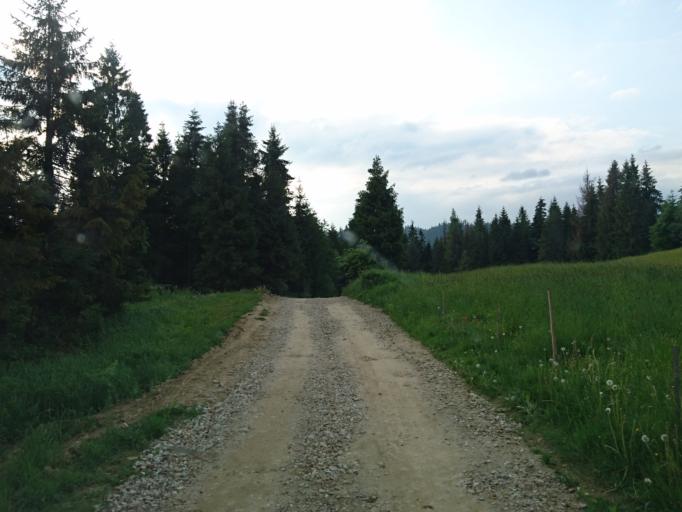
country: PL
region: Lesser Poland Voivodeship
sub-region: Powiat nowotarski
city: Lopuszna
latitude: 49.5046
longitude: 20.1873
